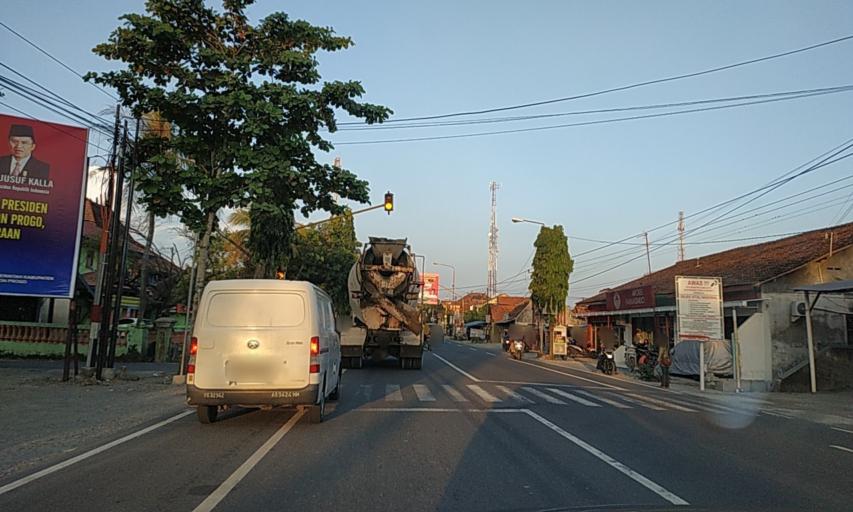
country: ID
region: Daerah Istimewa Yogyakarta
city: Srandakan
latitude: -7.8869
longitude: 110.0763
